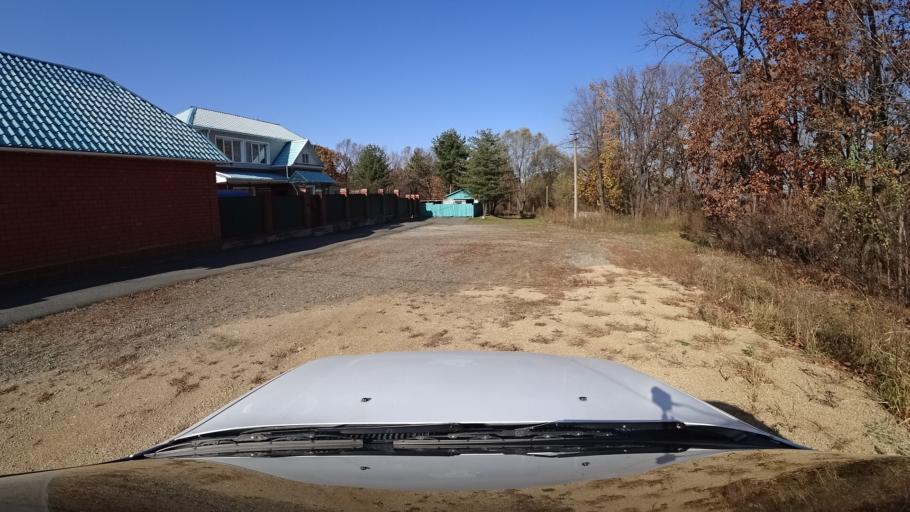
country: RU
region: Primorskiy
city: Dal'nerechensk
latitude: 45.8833
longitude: 133.7290
